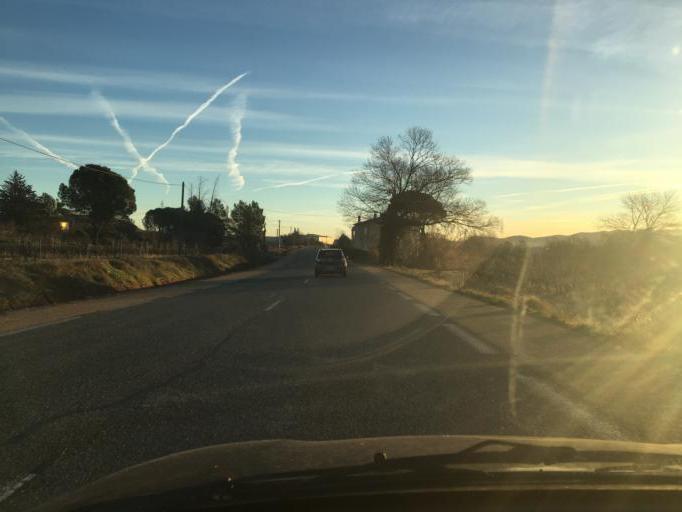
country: FR
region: Provence-Alpes-Cote d'Azur
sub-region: Departement du Var
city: Les Arcs
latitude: 43.4502
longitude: 6.4563
